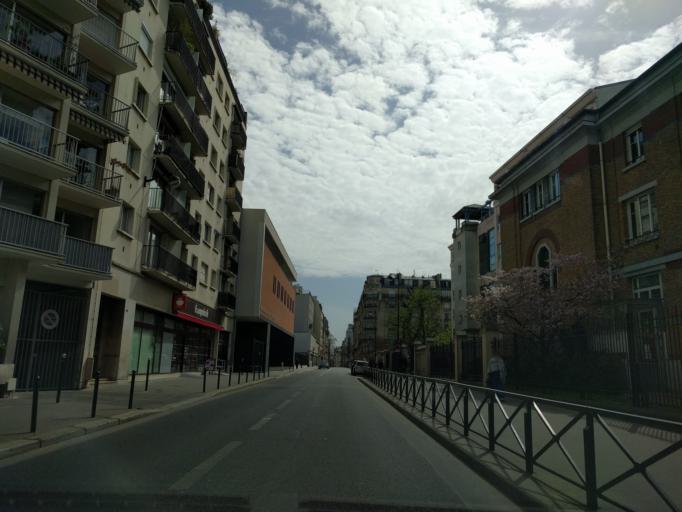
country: FR
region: Ile-de-France
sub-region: Departement du Val-de-Marne
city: Saint-Mande
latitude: 48.8422
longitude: 2.3980
